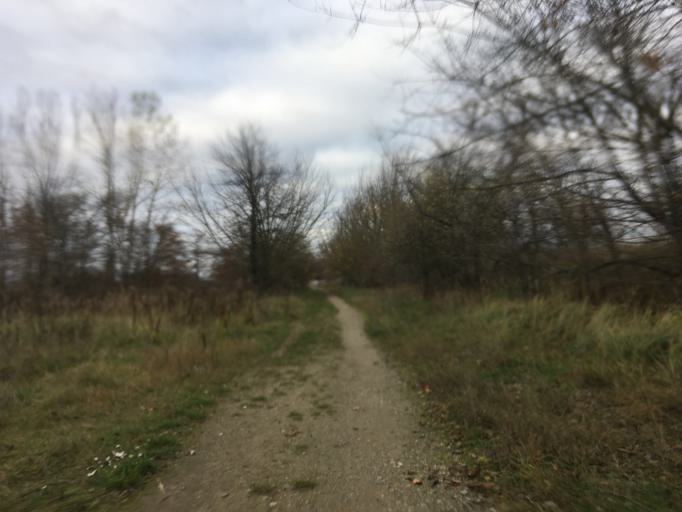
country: DE
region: Berlin
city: Bohnsdorf
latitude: 52.3946
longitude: 13.5530
